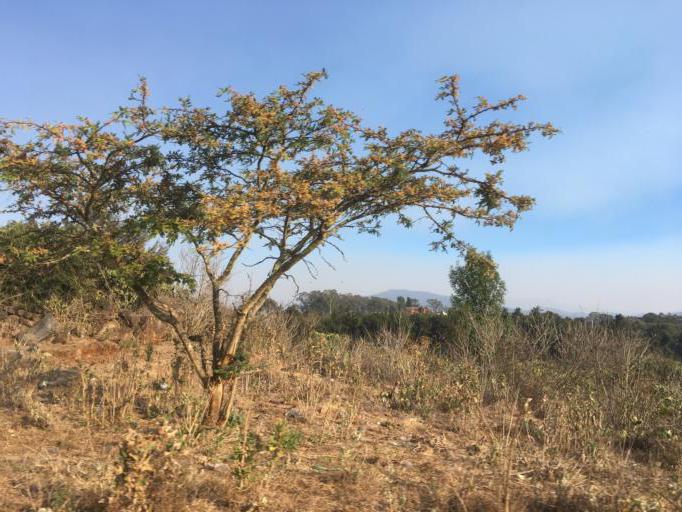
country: MX
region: Michoacan
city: Santa Fe de la Laguna
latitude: 19.6820
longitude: -101.5782
